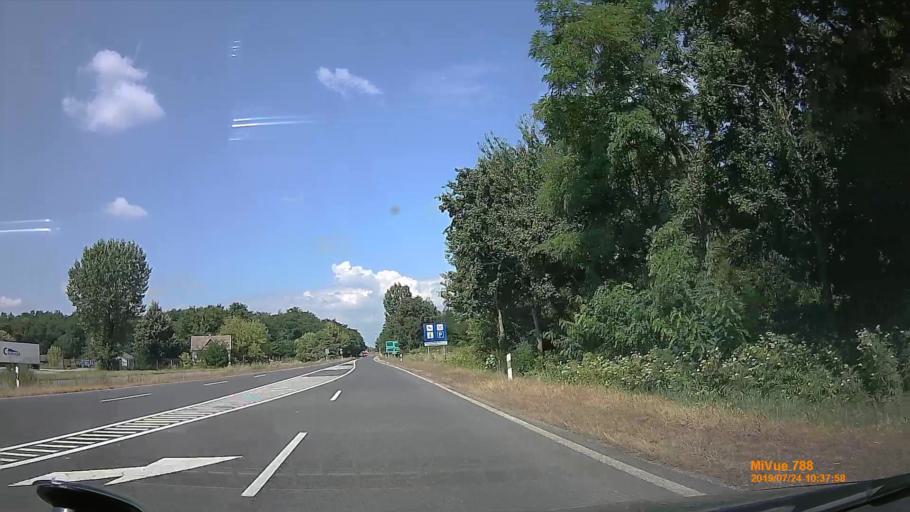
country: HU
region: Szabolcs-Szatmar-Bereg
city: Tarpa
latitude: 48.1587
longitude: 22.5484
